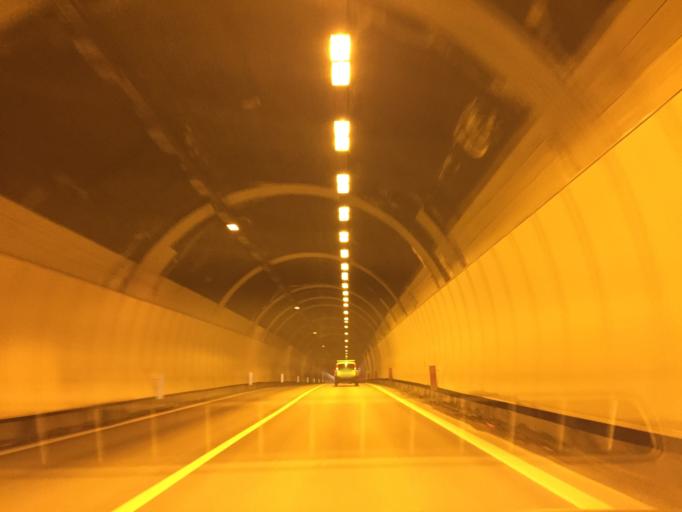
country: IT
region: Molise
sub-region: Provincia di Campobasso
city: Vinchiaturo
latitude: 41.5139
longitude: 14.6087
